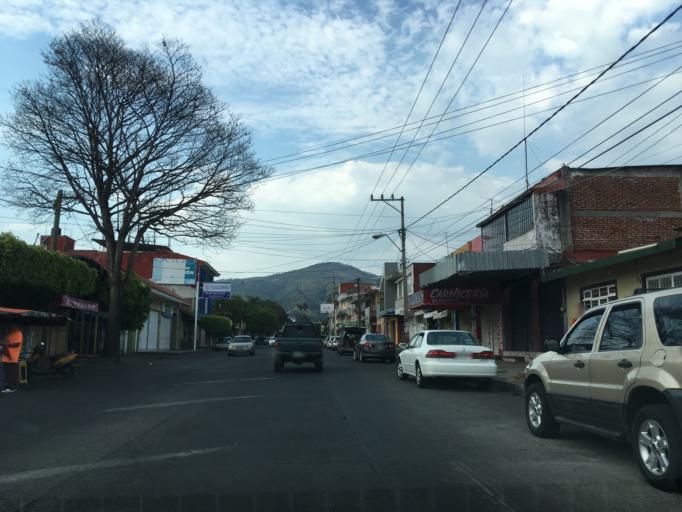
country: MX
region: Michoacan
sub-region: Uruapan
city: Uruapan
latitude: 19.4117
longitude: -102.0577
